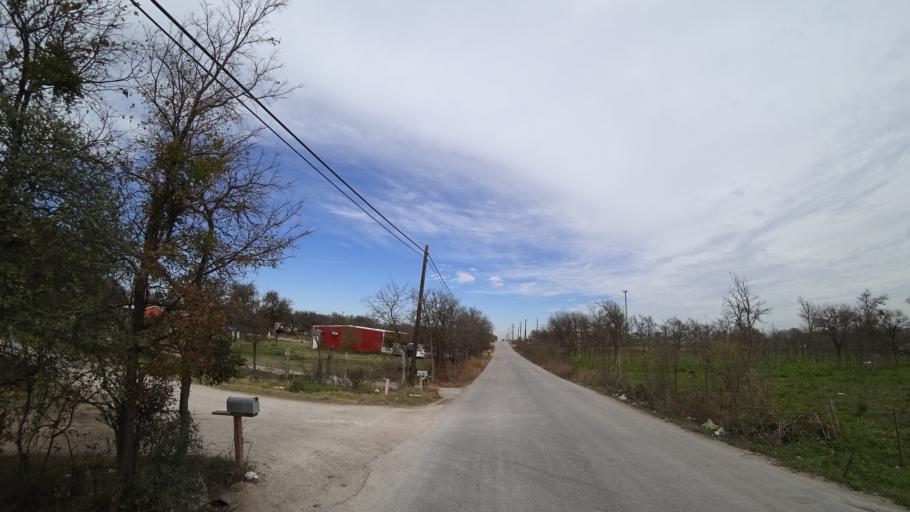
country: US
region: Texas
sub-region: Travis County
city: Garfield
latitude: 30.1379
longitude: -97.5693
